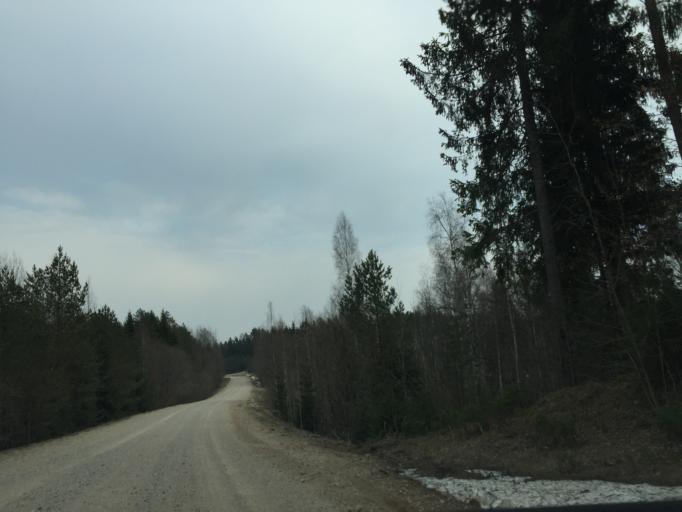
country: LV
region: Raunas
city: Rauna
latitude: 57.1632
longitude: 25.5207
